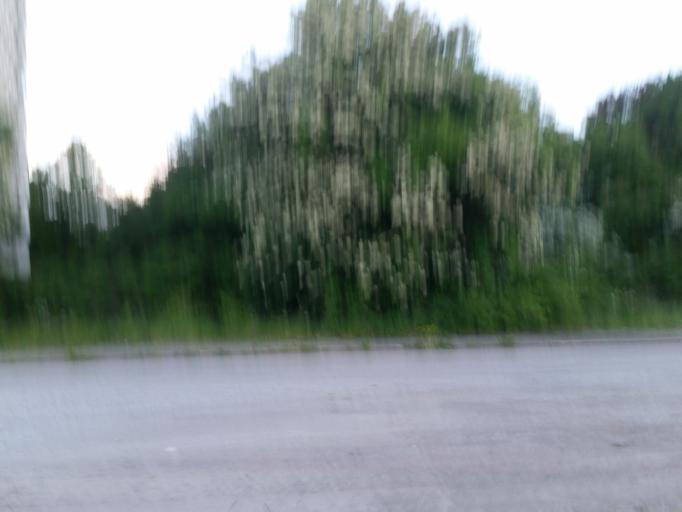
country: SE
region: Stockholm
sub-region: Stockholms Kommun
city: Arsta
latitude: 59.2916
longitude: 18.0537
